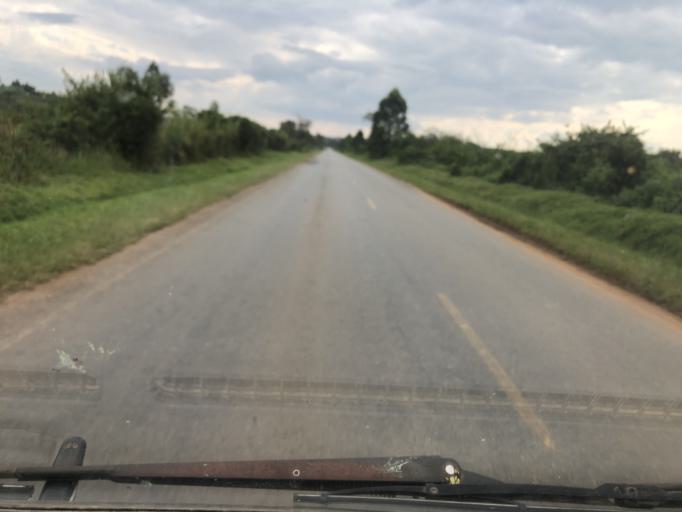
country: UG
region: Western Region
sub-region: Sheema District
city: Kibingo
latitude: -0.5801
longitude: 30.4323
